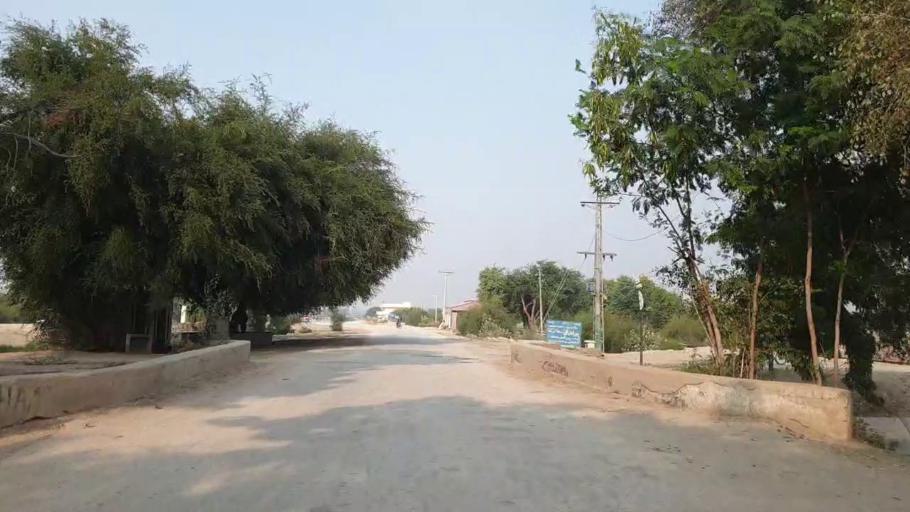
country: PK
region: Sindh
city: Bhan
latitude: 26.5871
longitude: 67.7293
